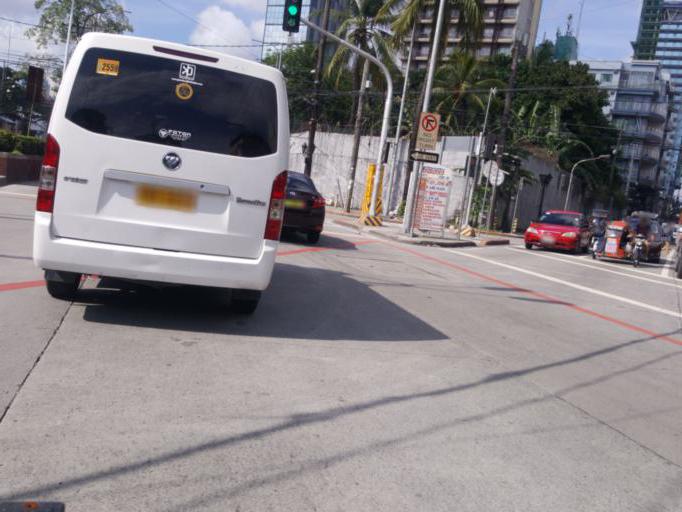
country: PH
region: Metro Manila
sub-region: City of Manila
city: Manila
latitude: 14.6097
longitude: 120.9862
